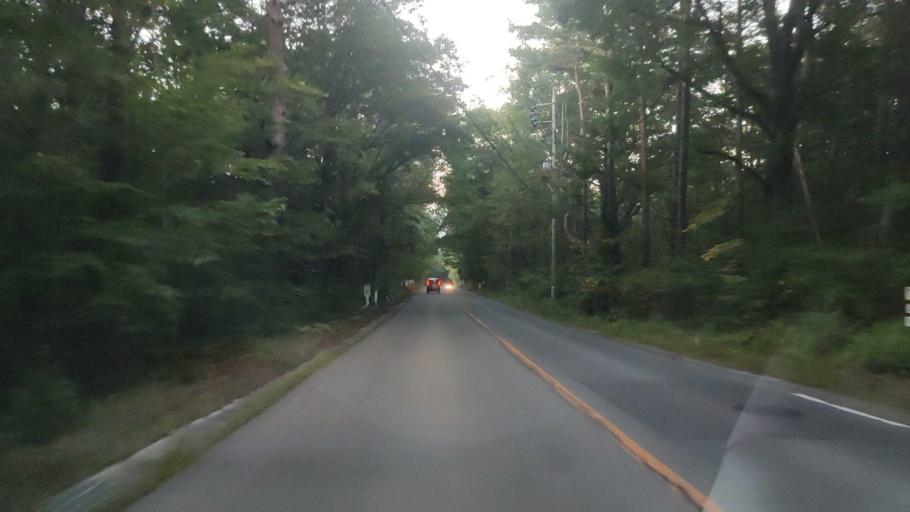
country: JP
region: Nagano
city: Komoro
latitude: 36.4496
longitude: 138.5819
